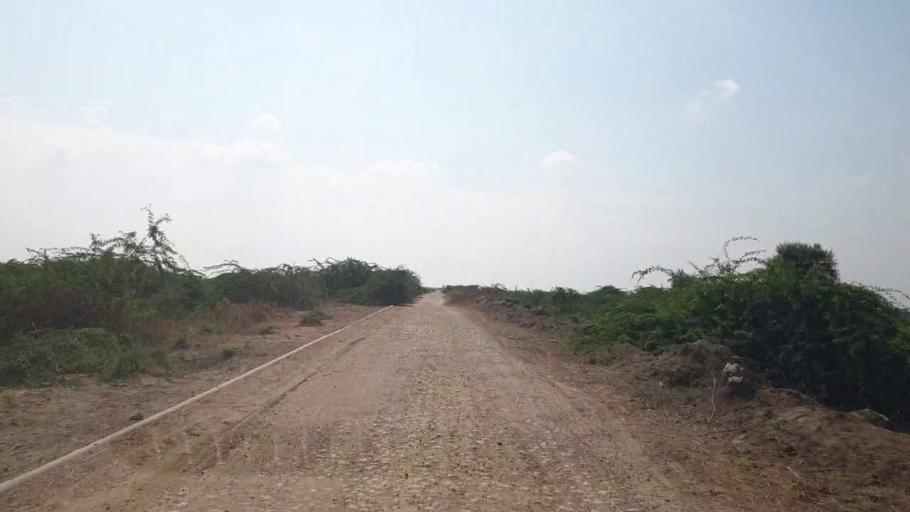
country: PK
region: Sindh
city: Badin
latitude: 24.5122
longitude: 68.6081
